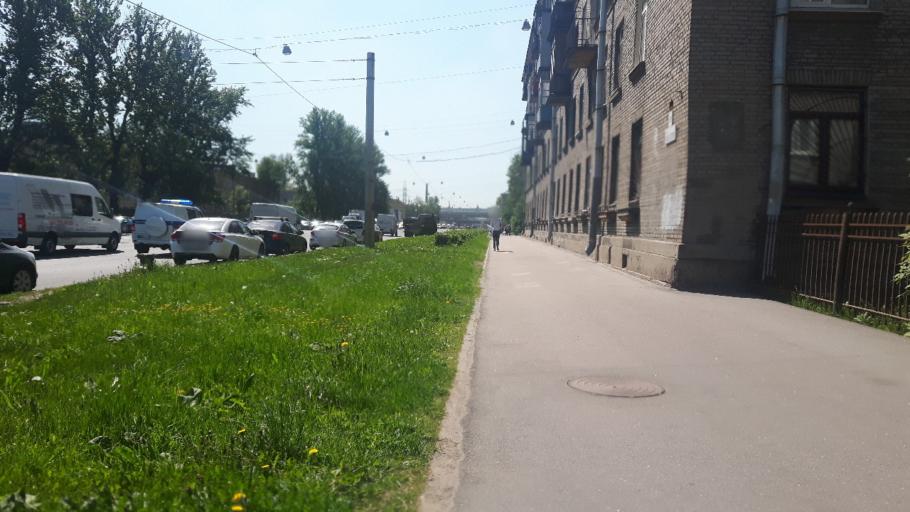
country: RU
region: St.-Petersburg
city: Avtovo
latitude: 59.8888
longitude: 30.2767
